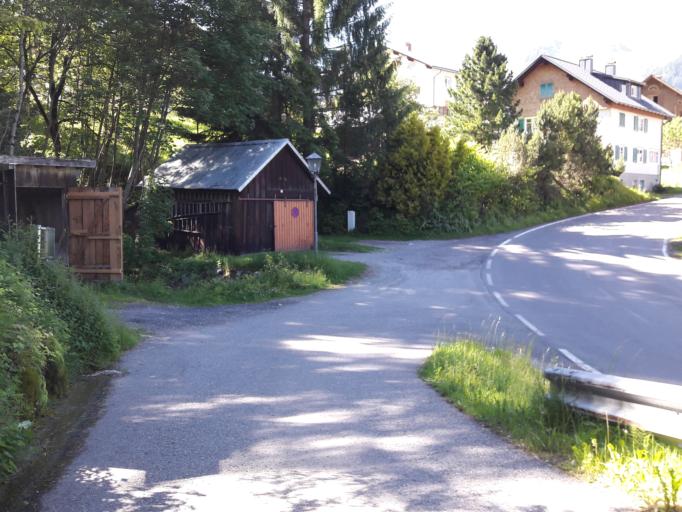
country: AT
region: Vorarlberg
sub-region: Politischer Bezirk Bludenz
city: Raggal
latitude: 47.2095
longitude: 9.8442
